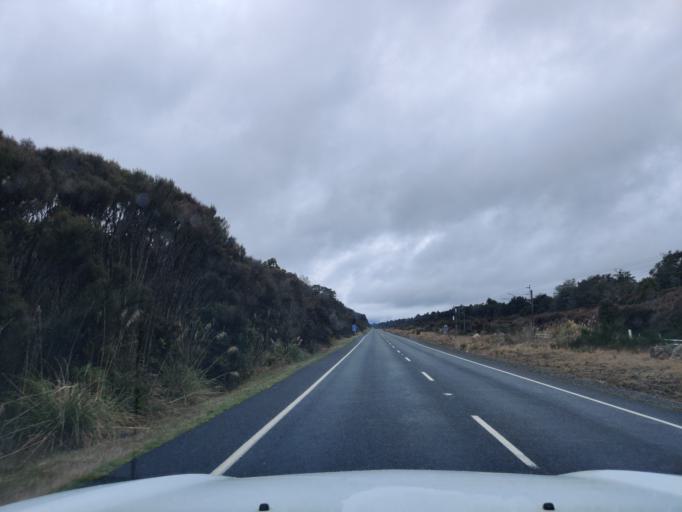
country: NZ
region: Manawatu-Wanganui
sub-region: Ruapehu District
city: Waiouru
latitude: -39.3171
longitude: 175.3870
